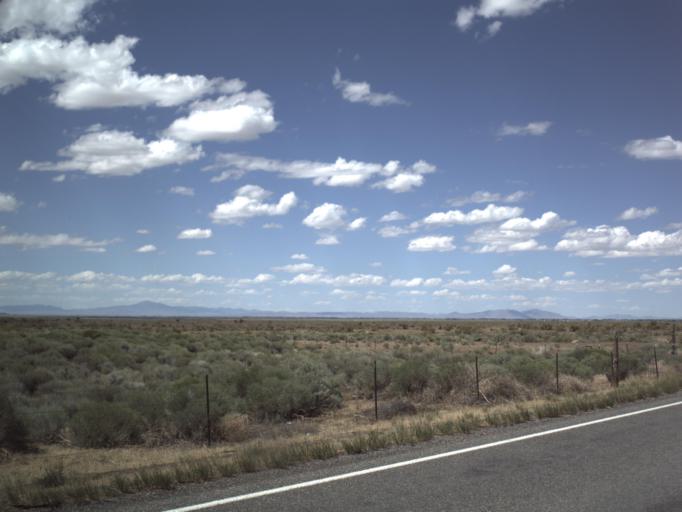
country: US
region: Utah
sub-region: Millard County
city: Delta
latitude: 39.2156
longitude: -112.4175
